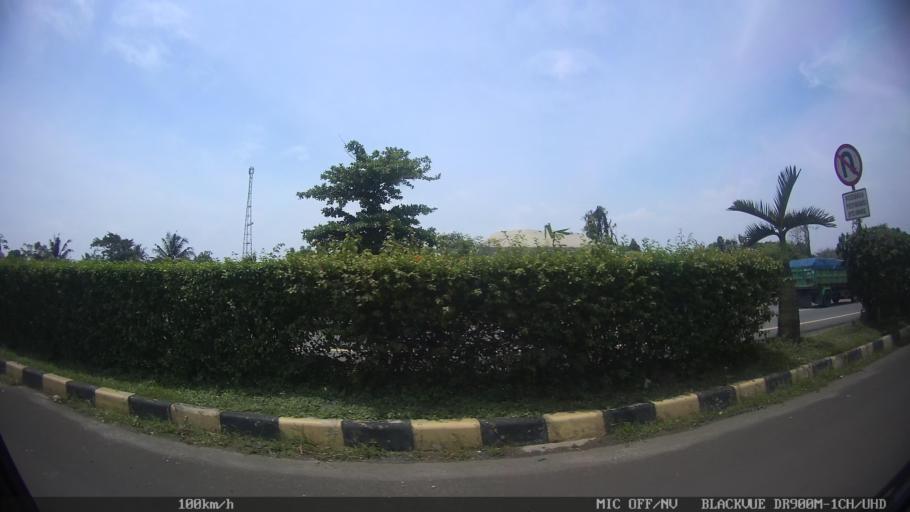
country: ID
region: West Java
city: Kresek
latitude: -6.1810
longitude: 106.3926
